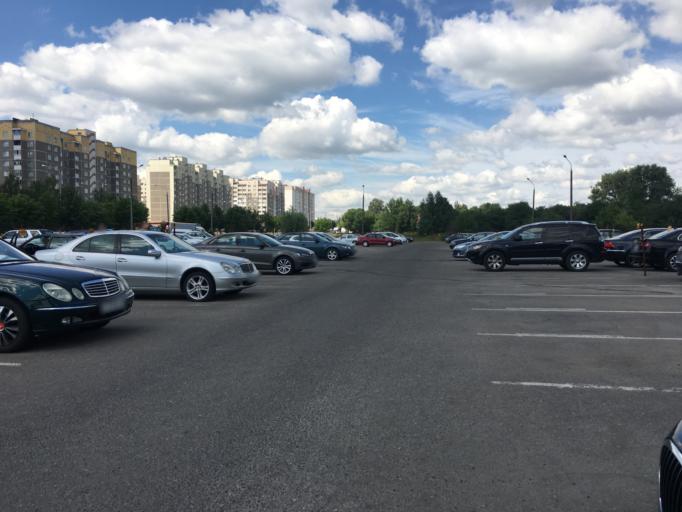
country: BY
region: Grodnenskaya
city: Hrodna
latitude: 53.7166
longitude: 23.8491
